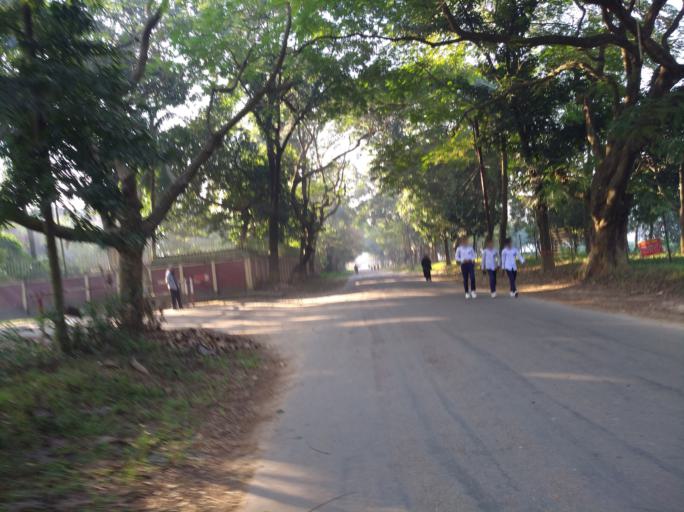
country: BD
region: Dhaka
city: Tungi
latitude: 23.8890
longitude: 90.2679
